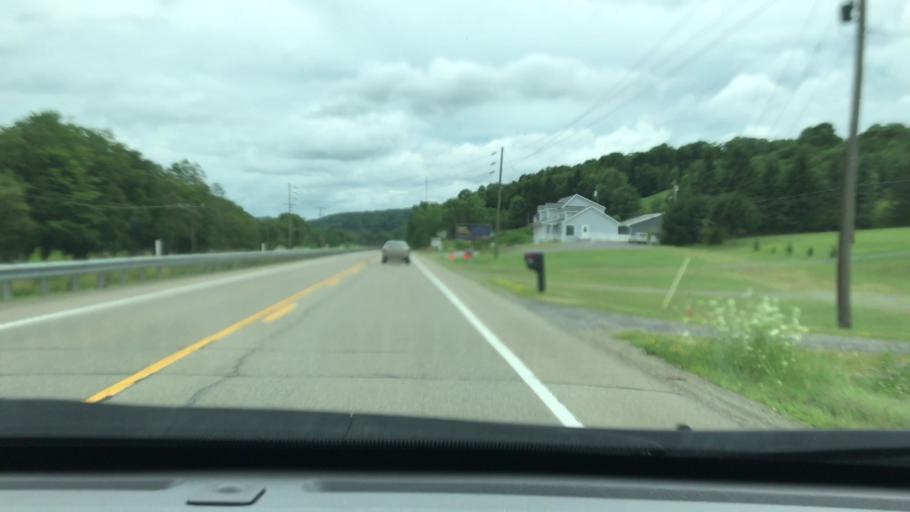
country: US
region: Pennsylvania
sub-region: Elk County
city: Johnsonburg
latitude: 41.5436
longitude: -78.6813
